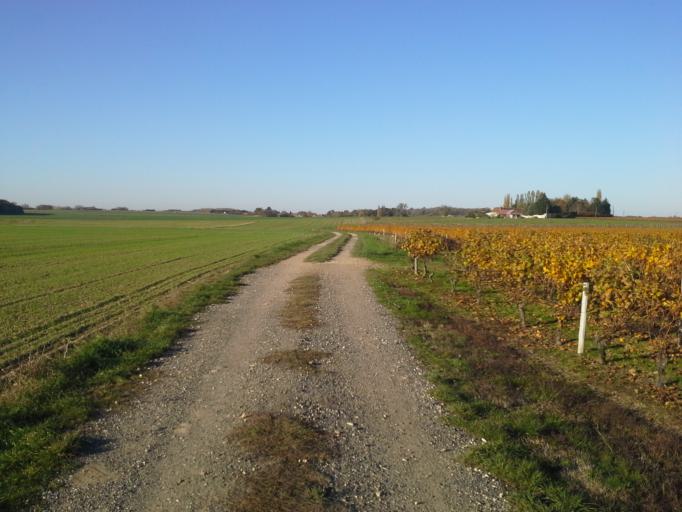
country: FR
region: Centre
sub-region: Departement du Loir-et-Cher
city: Saint-Romain-sur-Cher
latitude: 47.3678
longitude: 1.3970
